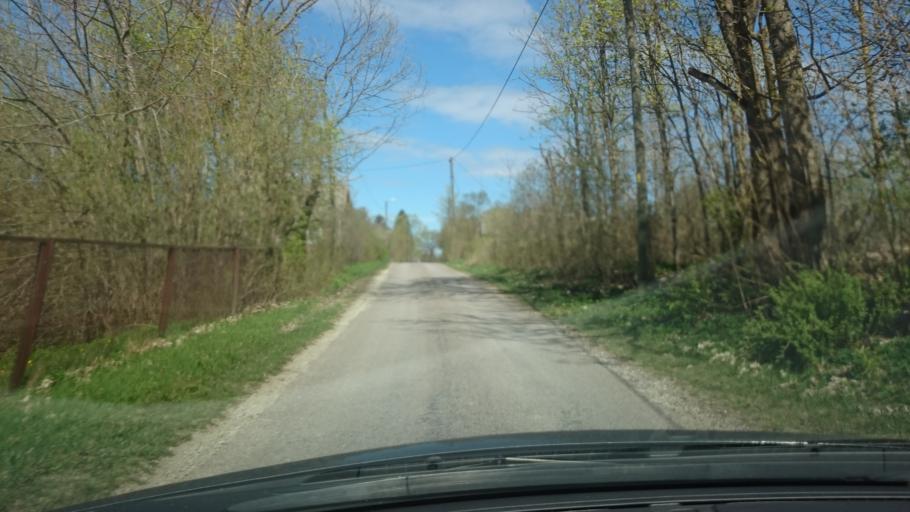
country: EE
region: Ida-Virumaa
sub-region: Sillamaee linn
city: Sillamae
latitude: 59.1189
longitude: 27.7994
